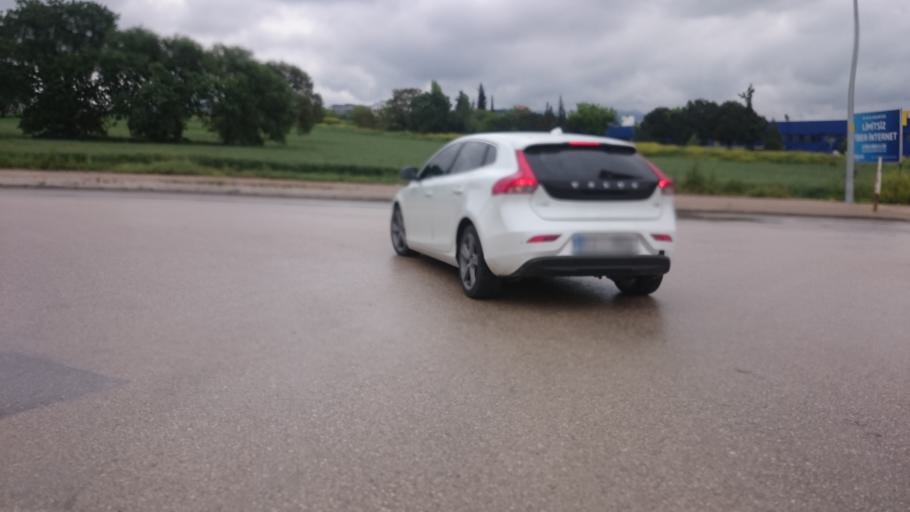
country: TR
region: Bursa
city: Cali
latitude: 40.2151
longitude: 28.9436
